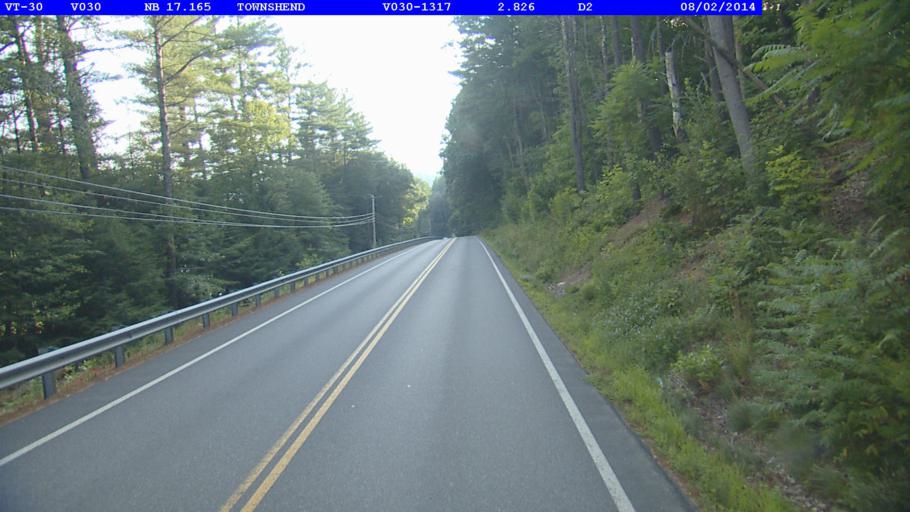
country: US
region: Vermont
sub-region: Windham County
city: Newfane
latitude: 43.0477
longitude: -72.6829
